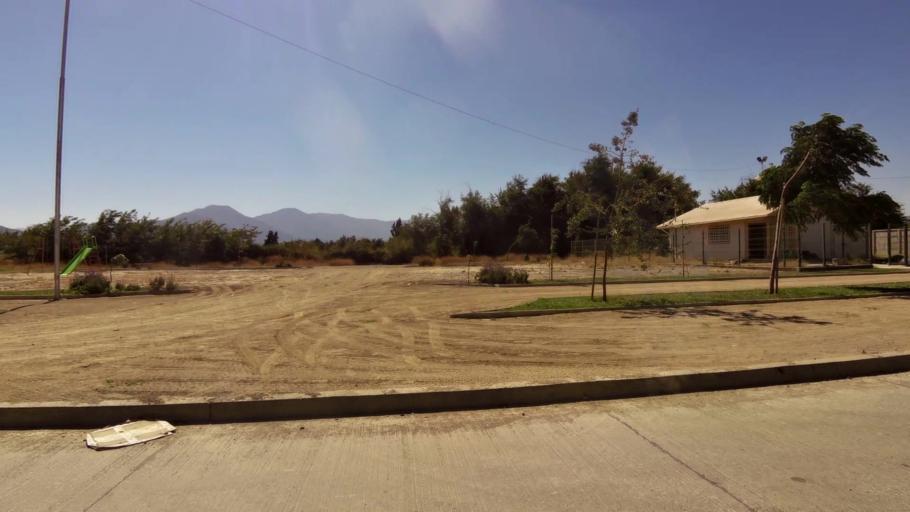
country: CL
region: O'Higgins
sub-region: Provincia de Cachapoal
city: Rancagua
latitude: -34.1774
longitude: -70.7776
